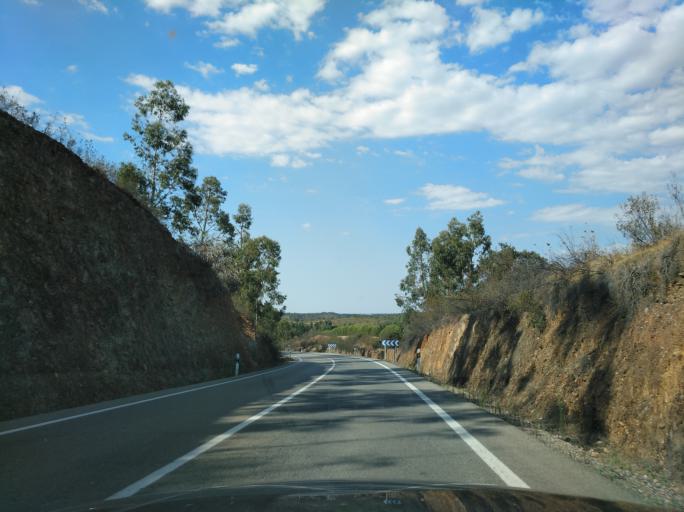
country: ES
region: Andalusia
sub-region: Provincia de Huelva
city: Santa Barbara de Casa
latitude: 37.8359
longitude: -7.2054
